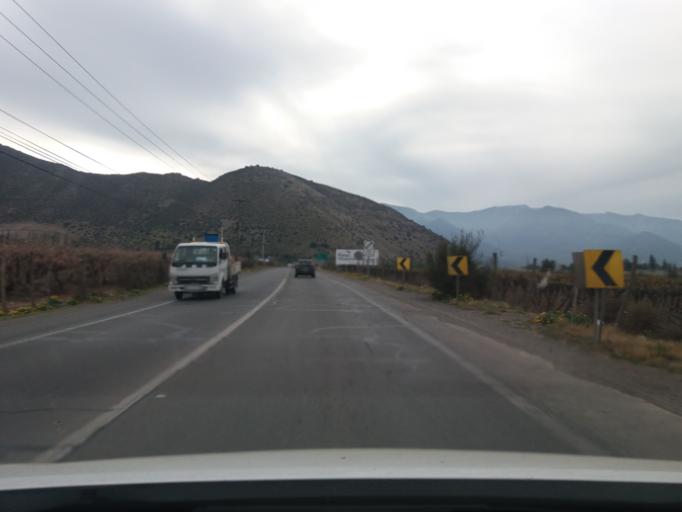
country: CL
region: Valparaiso
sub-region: Provincia de San Felipe
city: San Felipe
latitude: -32.7680
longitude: -70.7278
